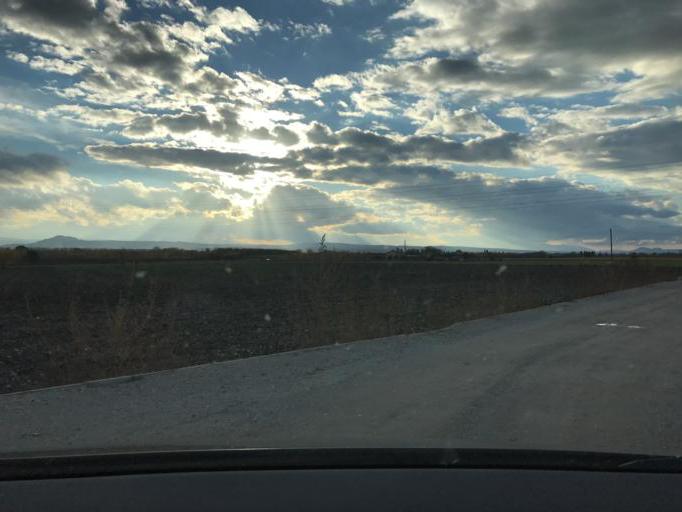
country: ES
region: Andalusia
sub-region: Provincia de Granada
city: Granada
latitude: 37.1744
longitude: -3.6226
